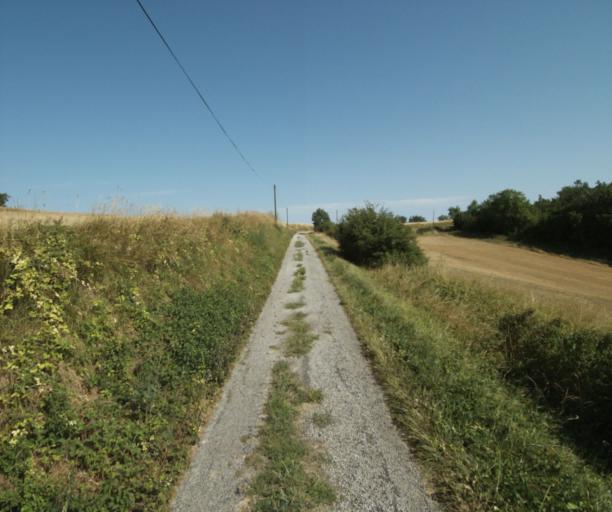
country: FR
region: Midi-Pyrenees
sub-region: Departement de la Haute-Garonne
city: Saint-Felix-Lauragais
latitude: 43.4302
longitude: 1.8460
